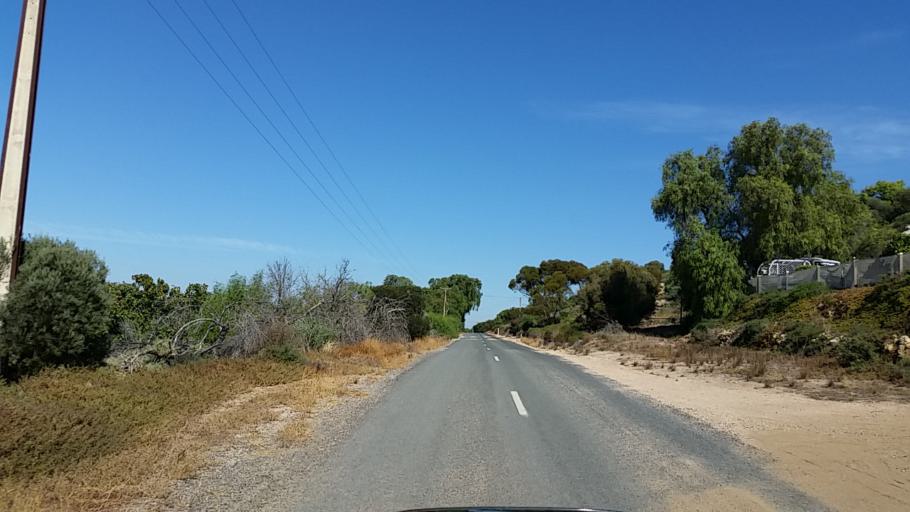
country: AU
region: South Australia
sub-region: Mid Murray
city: Mannum
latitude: -34.7020
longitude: 139.5725
